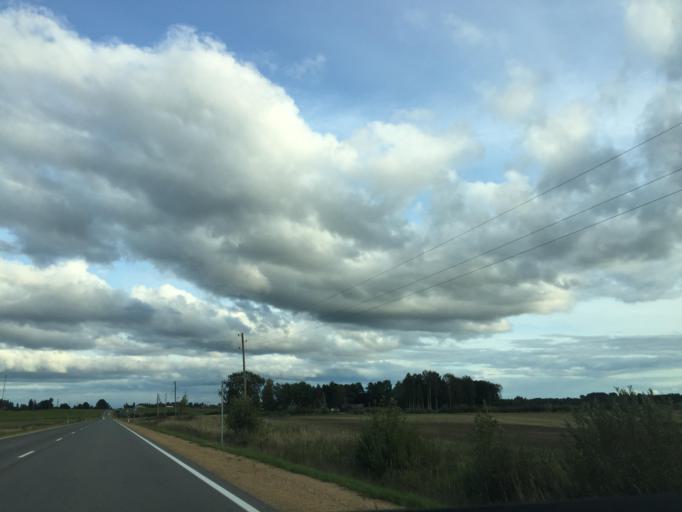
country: LV
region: Nereta
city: Nereta
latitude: 56.2188
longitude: 25.2917
